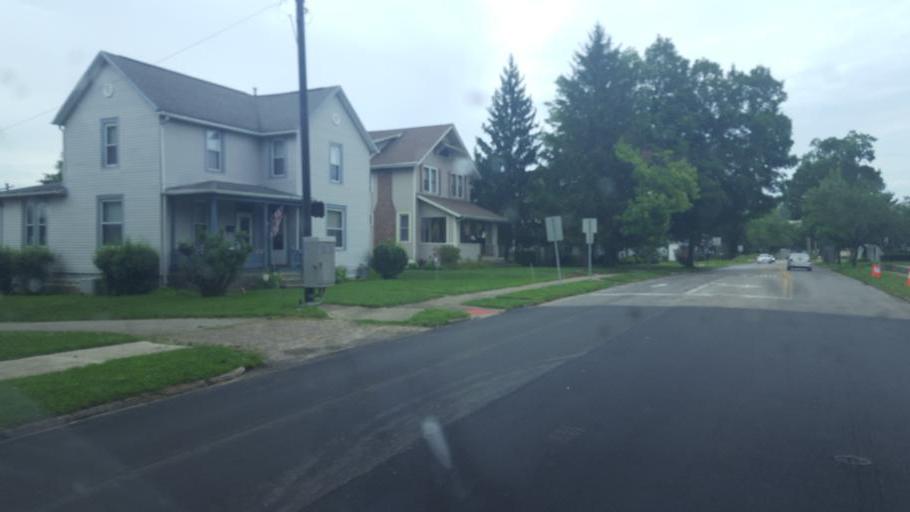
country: US
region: Ohio
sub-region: Pickaway County
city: Circleville
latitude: 39.6106
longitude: -82.9412
